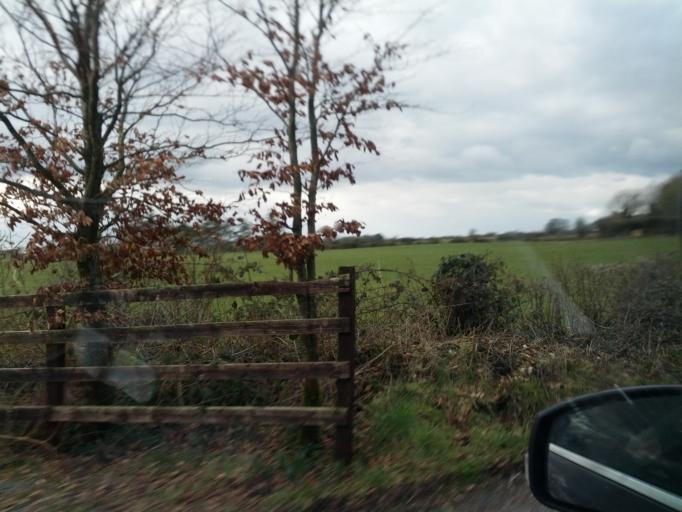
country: IE
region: Connaught
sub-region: County Galway
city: Athenry
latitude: 53.4919
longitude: -8.5953
